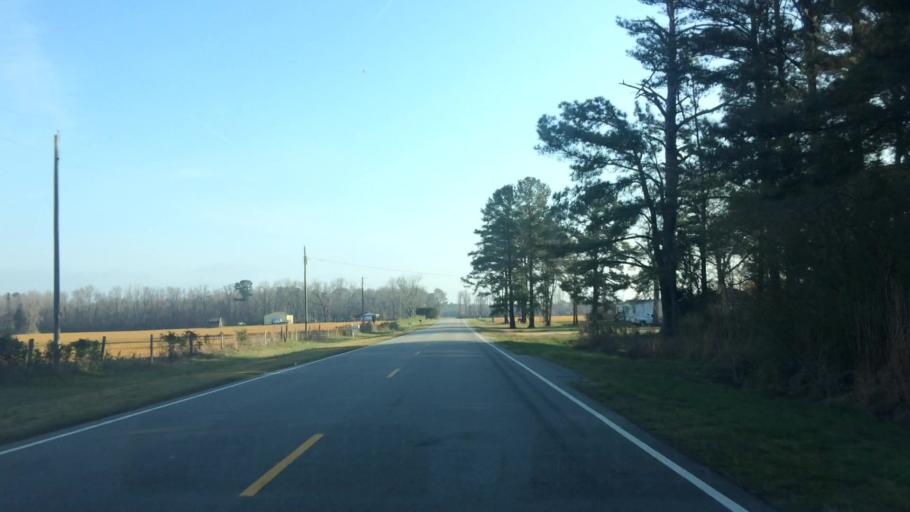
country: US
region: North Carolina
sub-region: Edgecombe County
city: Pinetops
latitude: 35.6954
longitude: -77.6381
